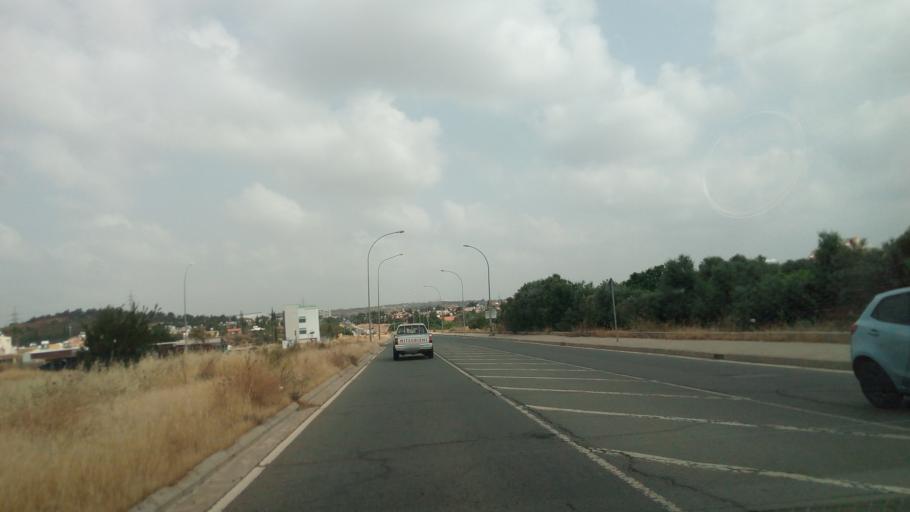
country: CY
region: Limassol
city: Pano Polemidia
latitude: 34.6927
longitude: 32.9885
